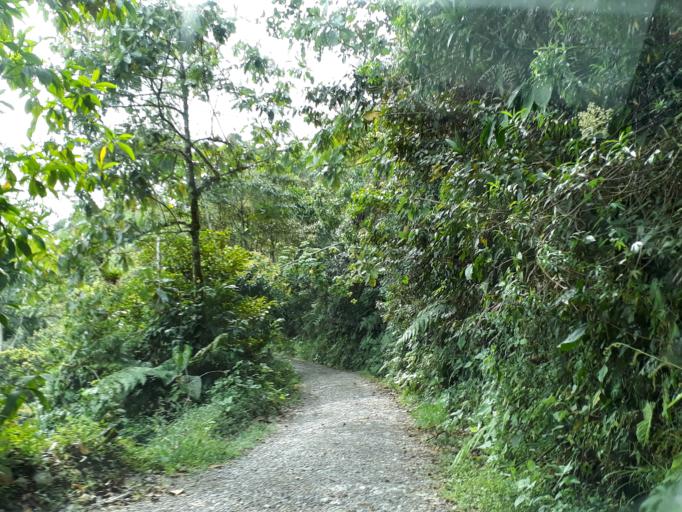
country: CO
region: Boyaca
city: Quipama
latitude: 5.3940
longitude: -74.1195
